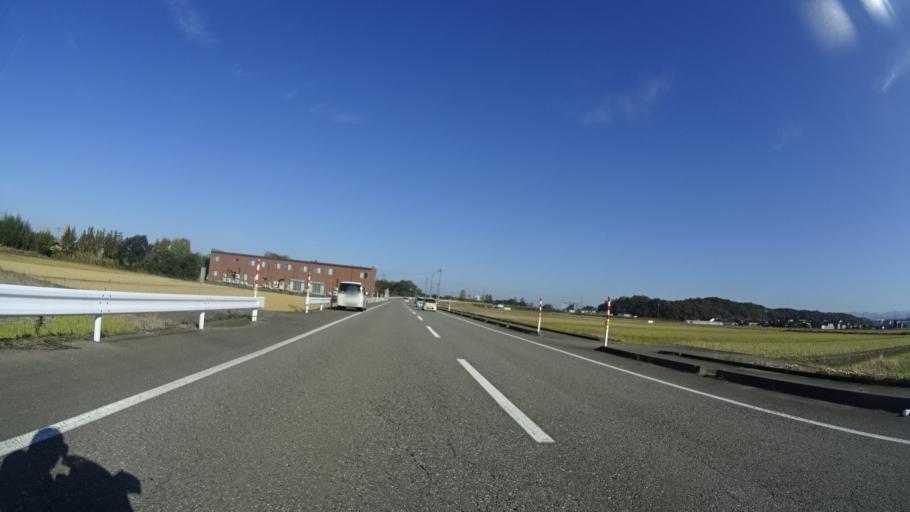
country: JP
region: Ishikawa
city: Komatsu
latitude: 36.3058
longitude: 136.3852
